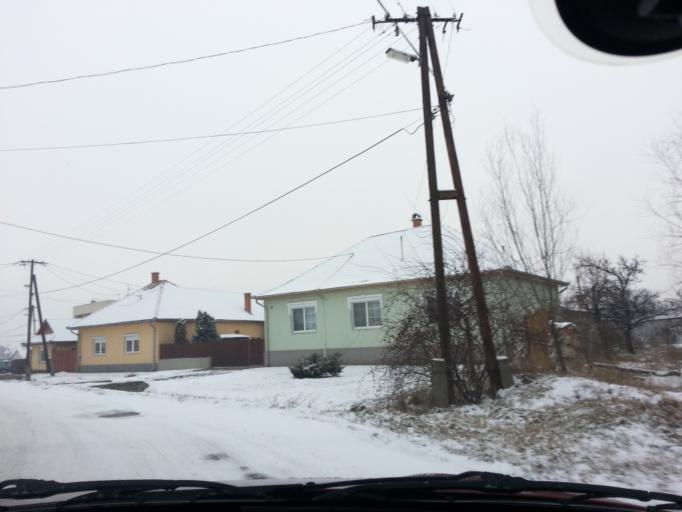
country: HU
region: Nograd
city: Paszto
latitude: 47.9158
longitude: 19.7023
